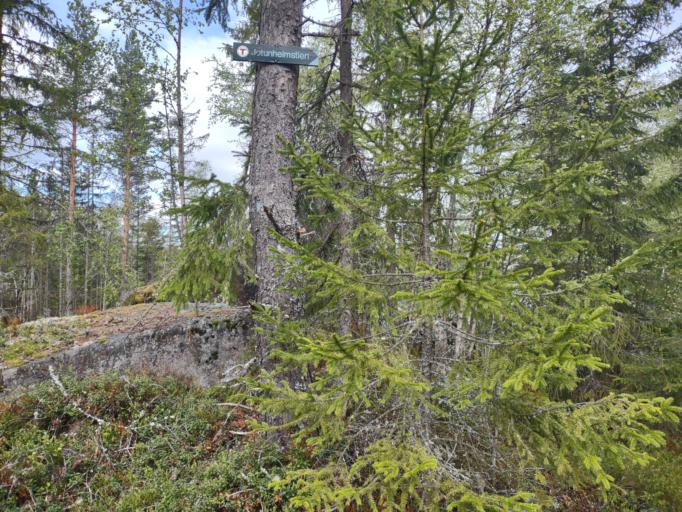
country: NO
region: Oppland
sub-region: Lunner
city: Grua
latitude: 60.2837
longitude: 10.7773
